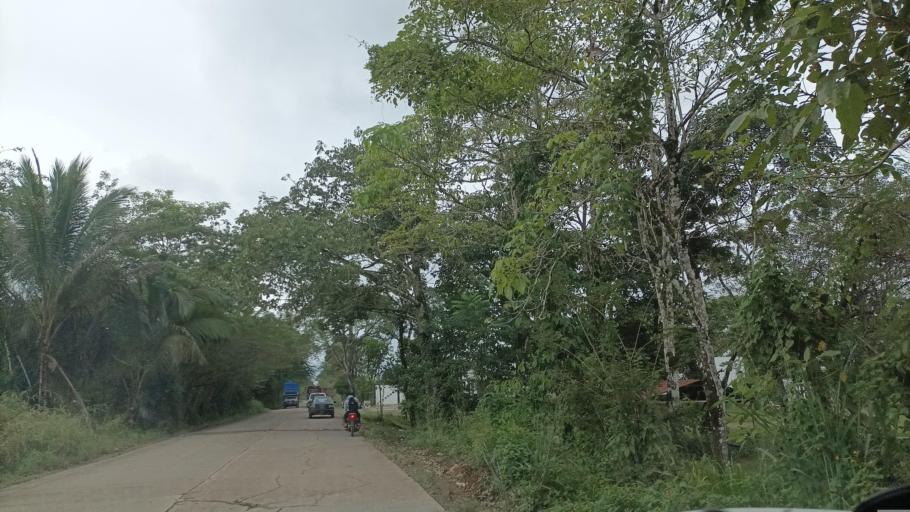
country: MX
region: Veracruz
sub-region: Uxpanapa
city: Poblado 10
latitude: 17.2773
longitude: -94.4624
